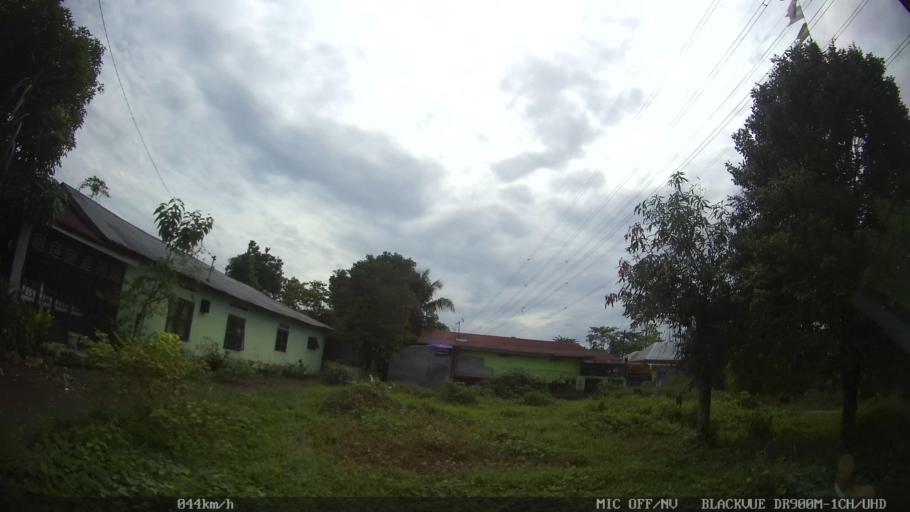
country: ID
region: North Sumatra
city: Sunggal
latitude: 3.5897
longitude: 98.5830
